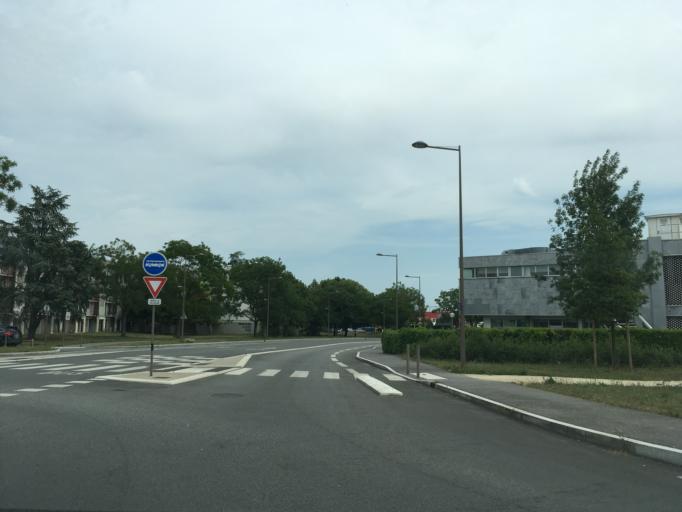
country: FR
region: Poitou-Charentes
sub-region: Departement des Deux-Sevres
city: Niort
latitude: 46.3132
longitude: -0.4816
